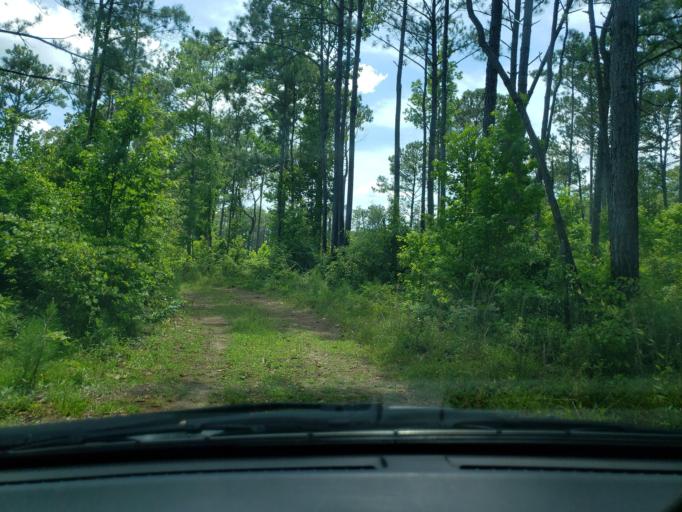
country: US
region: Alabama
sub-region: Elmore County
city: Eclectic
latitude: 32.6365
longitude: -85.9422
